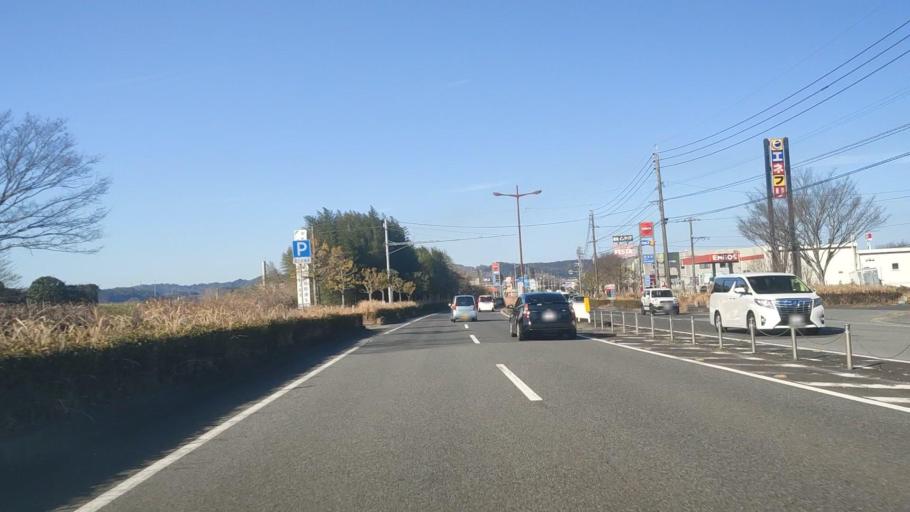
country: JP
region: Oita
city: Oita
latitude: 33.1392
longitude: 131.6584
